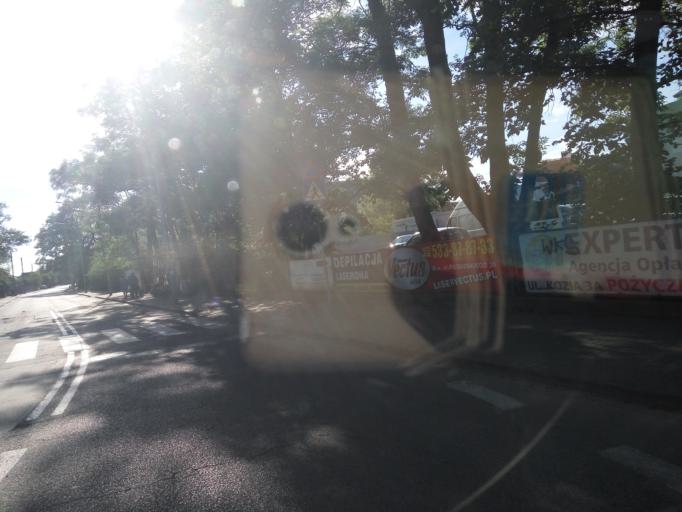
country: PL
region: Lower Silesian Voivodeship
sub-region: Powiat wroclawski
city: Smolec
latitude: 51.1576
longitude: 16.9339
